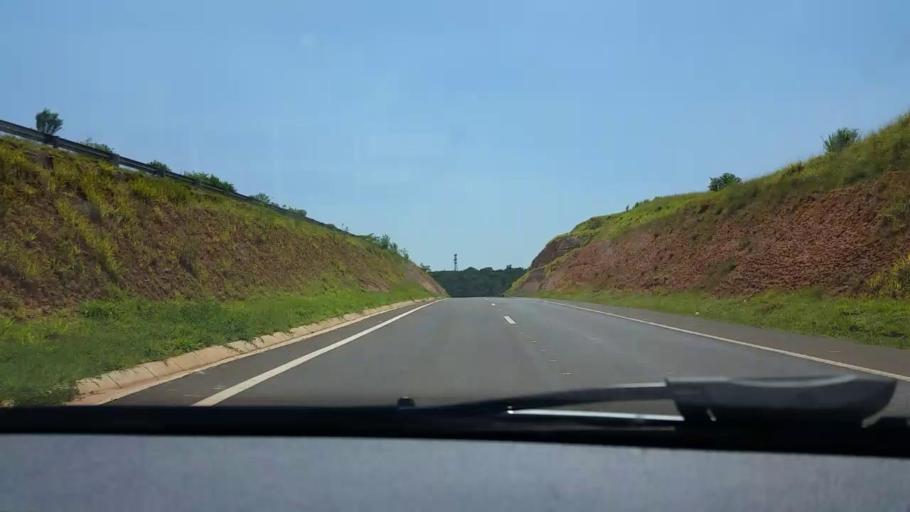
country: BR
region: Sao Paulo
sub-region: Bauru
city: Bauru
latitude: -22.4381
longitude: -49.1407
